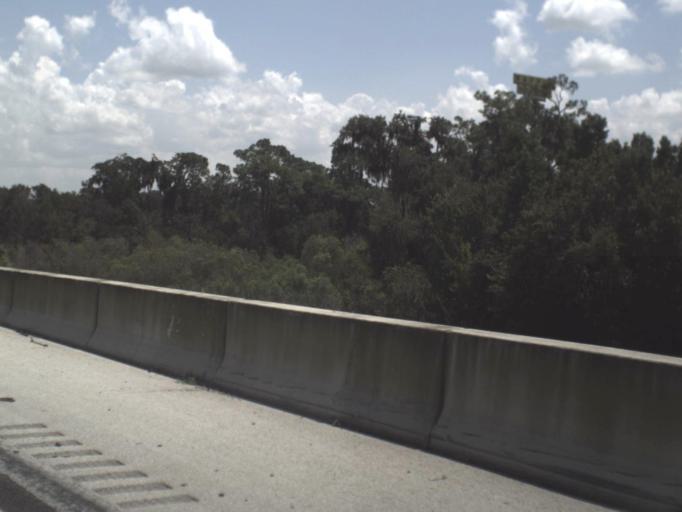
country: US
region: Florida
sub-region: Hillsborough County
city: Plant City
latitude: 28.0271
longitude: -82.1513
